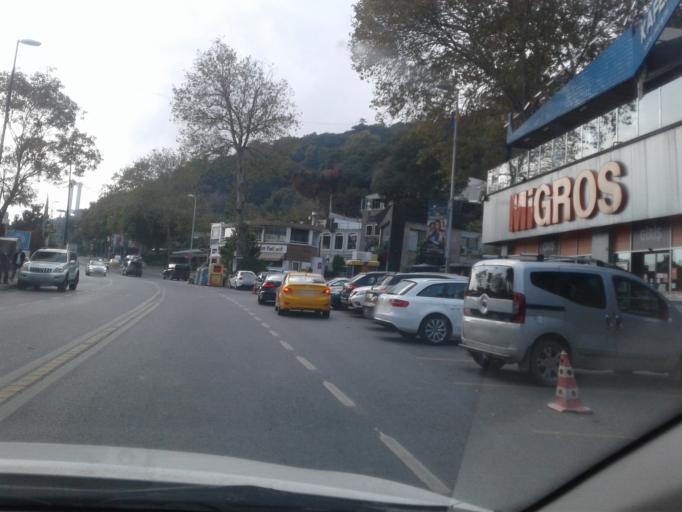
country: TR
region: Istanbul
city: UEskuedar
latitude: 41.0598
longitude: 29.0363
